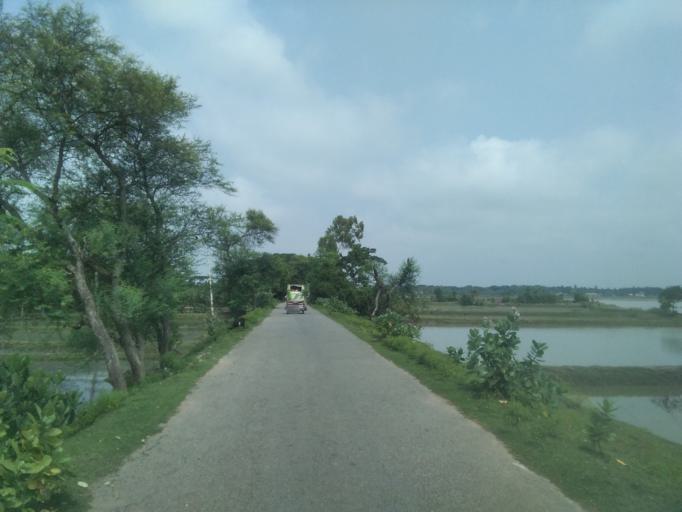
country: BD
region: Khulna
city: Phultala
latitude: 22.7049
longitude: 89.4641
